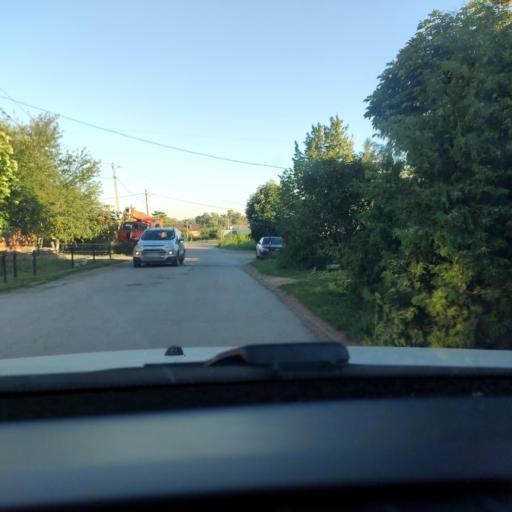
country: RU
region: Samara
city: Kinel'
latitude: 53.2695
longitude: 50.5927
